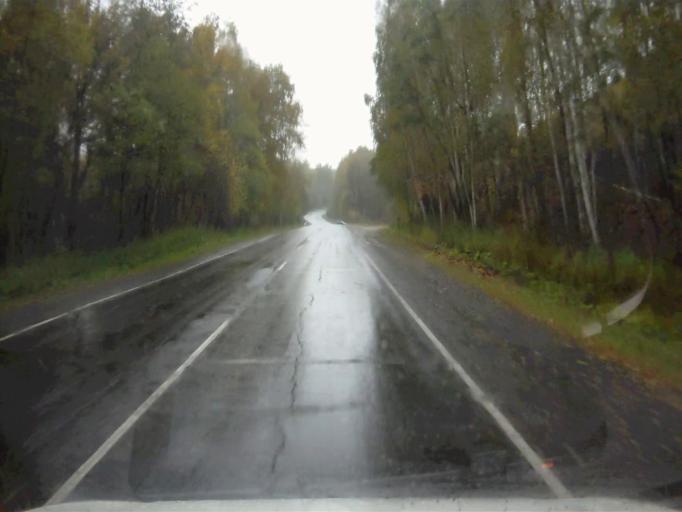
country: RU
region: Chelyabinsk
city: Kyshtym
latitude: 55.9096
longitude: 60.4361
